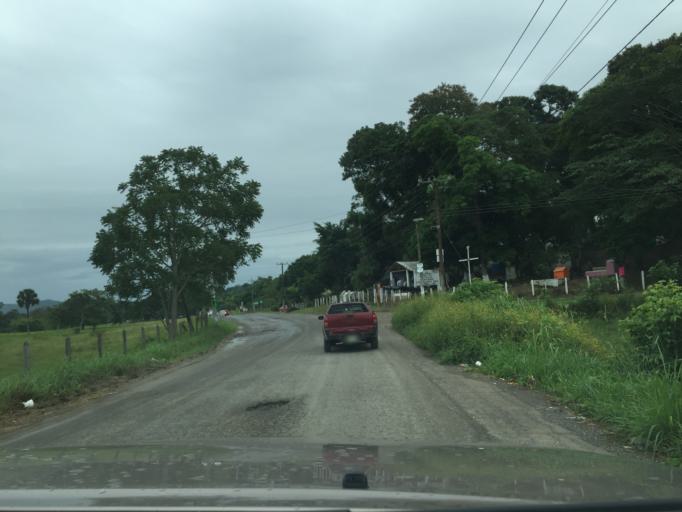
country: MX
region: Veracruz
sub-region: Papantla
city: El Chote
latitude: 20.4425
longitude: -97.4057
